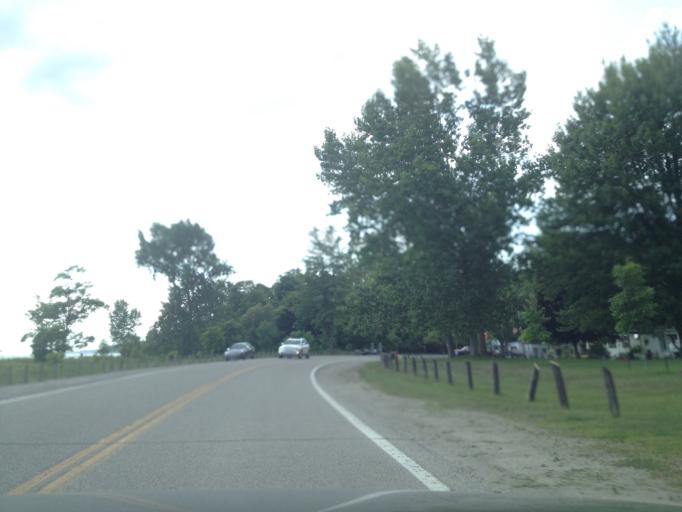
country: CA
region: Ontario
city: Aylmer
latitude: 42.6553
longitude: -81.0136
